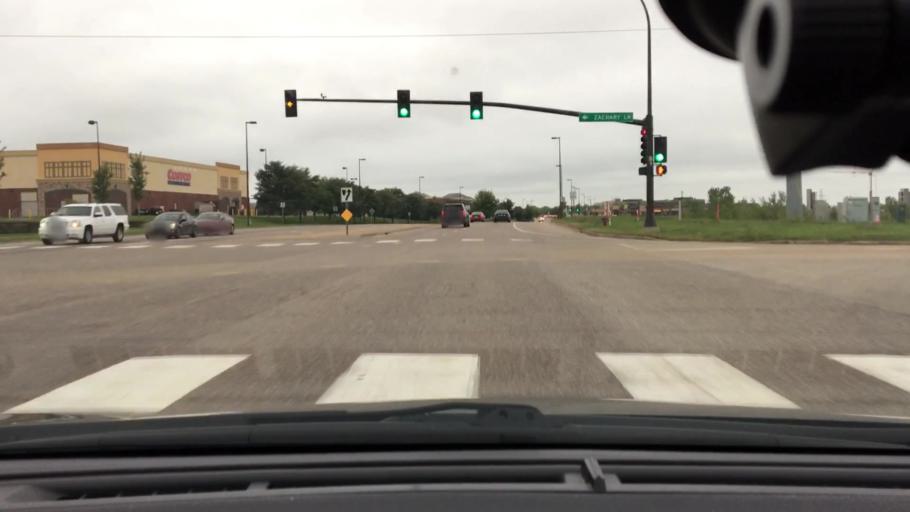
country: US
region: Minnesota
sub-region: Hennepin County
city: Osseo
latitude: 45.0946
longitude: -93.4216
